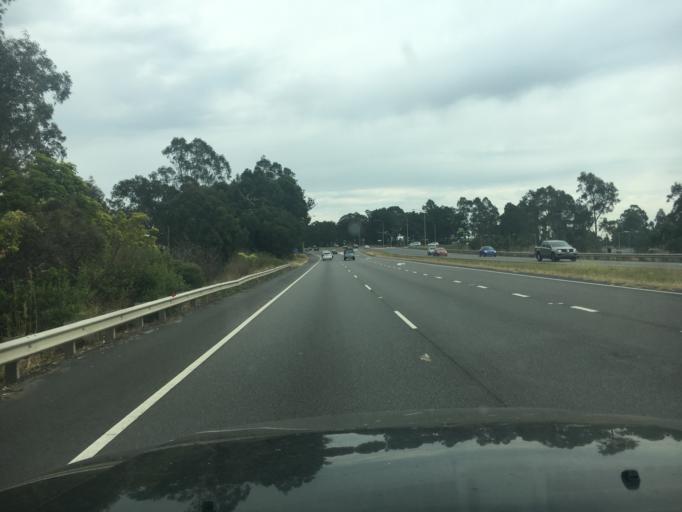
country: AU
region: New South Wales
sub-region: Maitland Municipality
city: East Maitland
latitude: -32.7771
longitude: 151.6139
